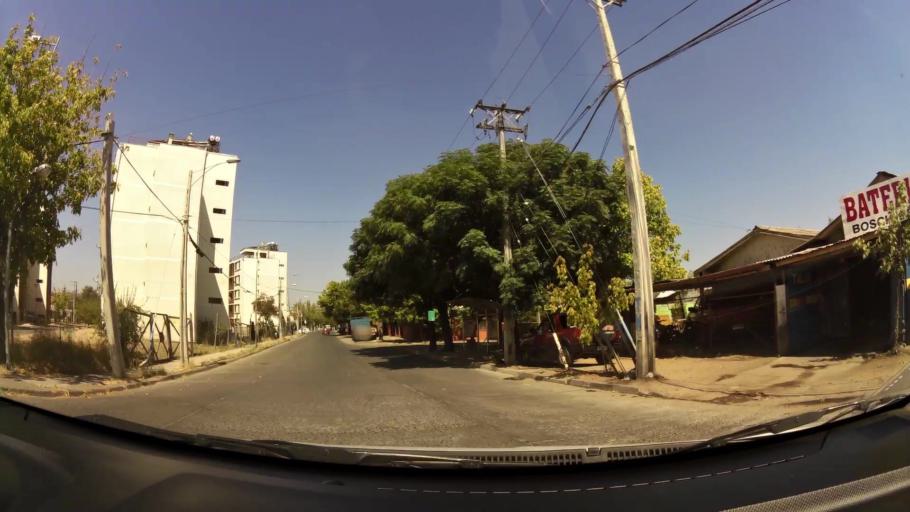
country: CL
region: Maule
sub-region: Provincia de Talca
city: Talca
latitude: -35.4139
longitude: -71.6532
